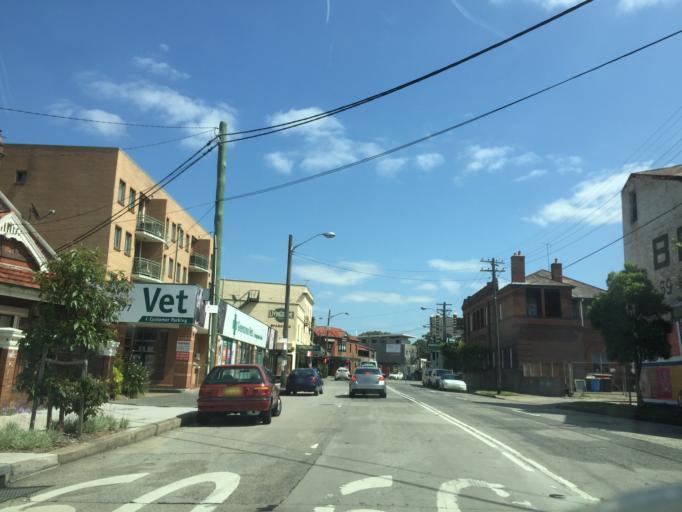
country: AU
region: New South Wales
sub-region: Marrickville
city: Lewisham
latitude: -33.8971
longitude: 151.1534
